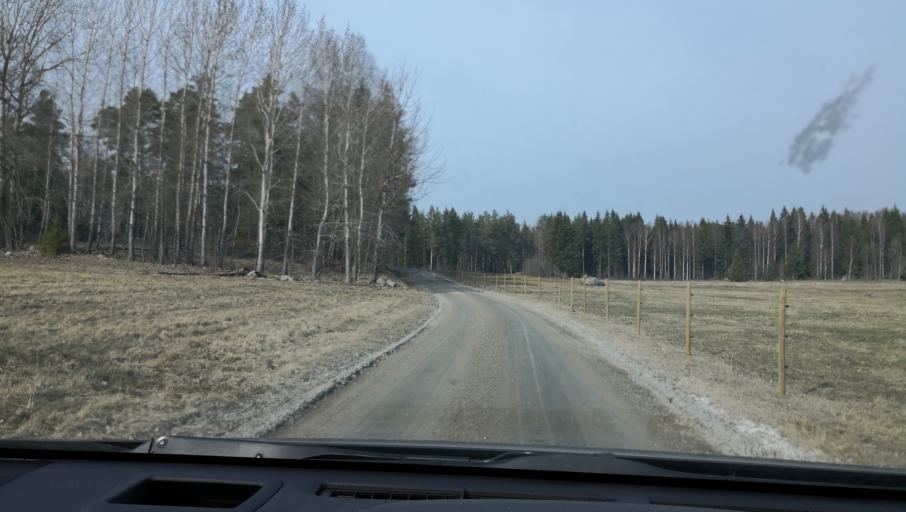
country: SE
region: OErebro
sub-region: Lindesbergs Kommun
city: Frovi
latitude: 59.3548
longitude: 15.4352
